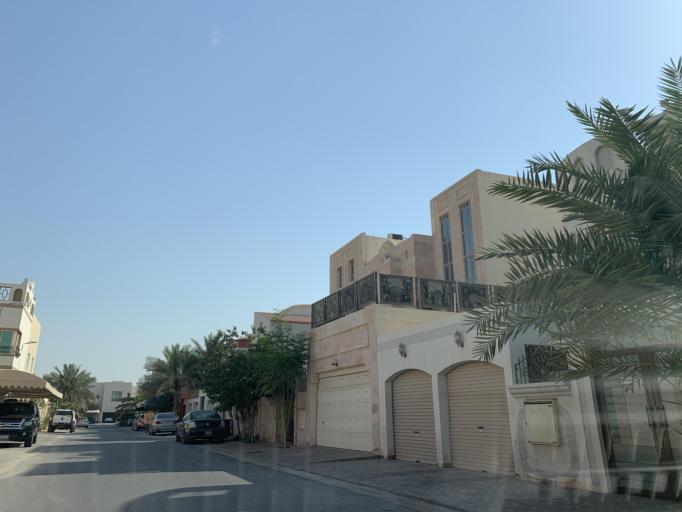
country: BH
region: Northern
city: Madinat `Isa
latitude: 26.1955
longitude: 50.5170
